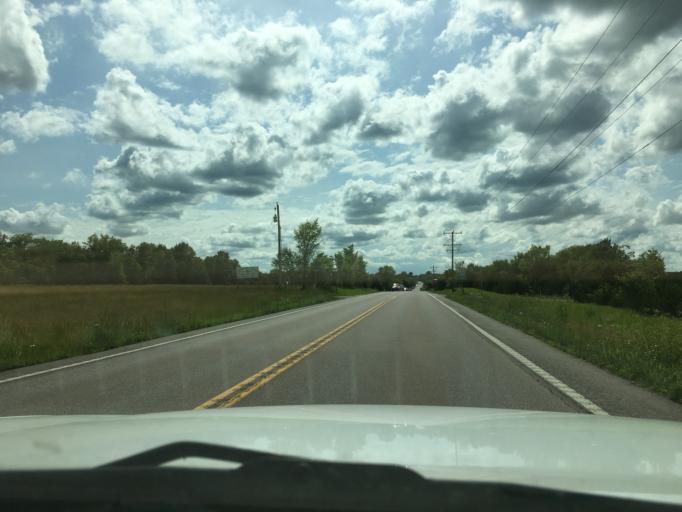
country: US
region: Missouri
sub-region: Franklin County
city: Gerald
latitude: 38.3874
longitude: -91.3895
